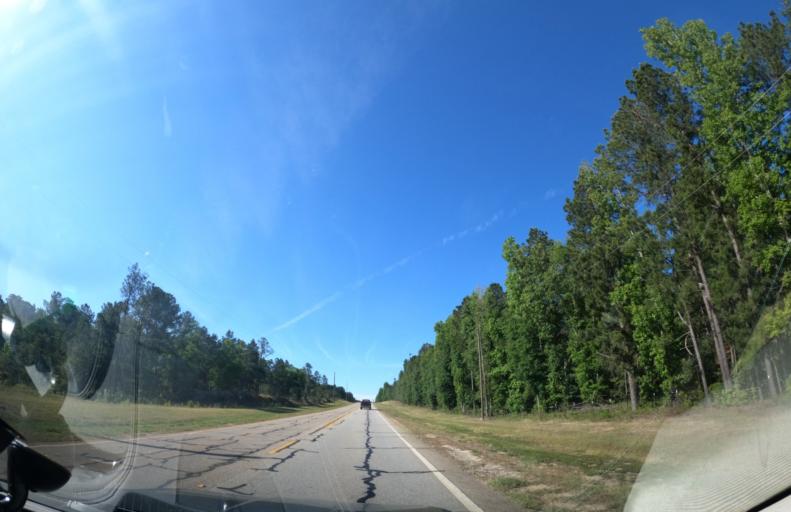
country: US
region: Georgia
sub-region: Jefferson County
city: Wrens
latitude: 33.3080
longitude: -82.3758
